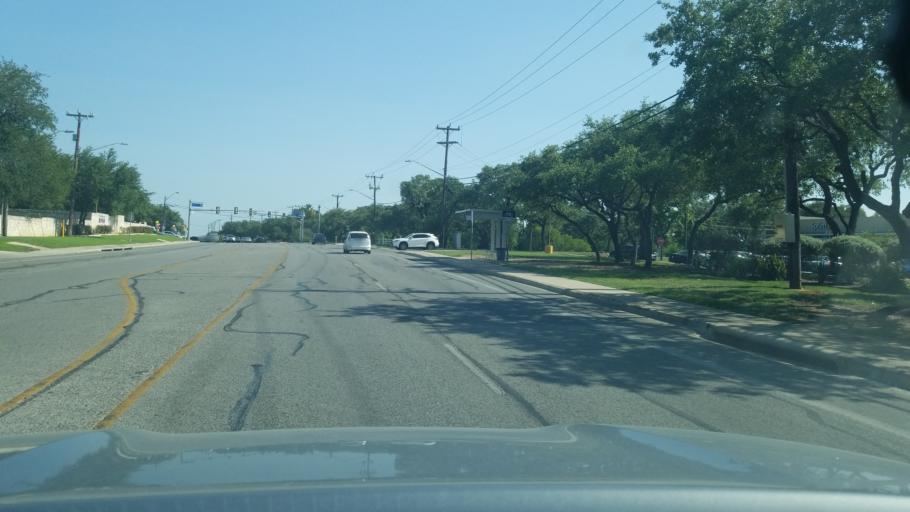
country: US
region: Texas
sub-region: Bexar County
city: Hollywood Park
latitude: 29.6065
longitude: -98.5084
